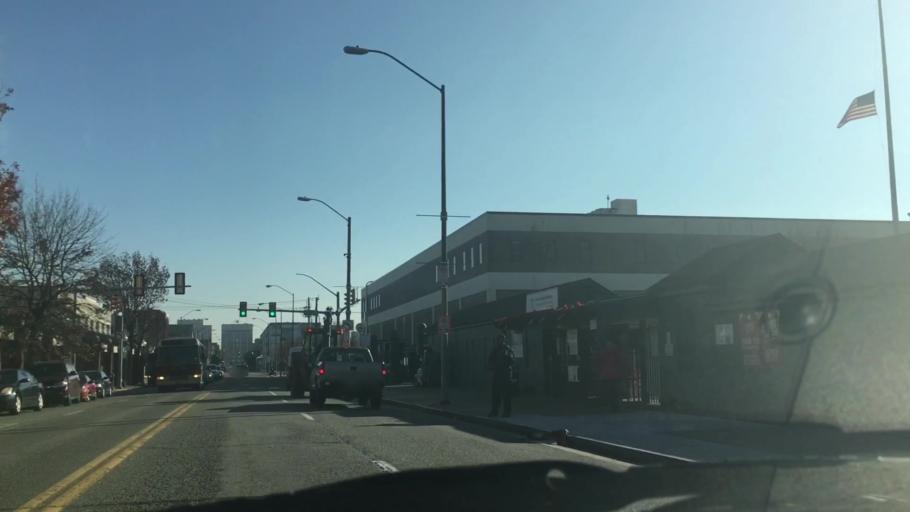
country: US
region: Virginia
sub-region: City of Newport News
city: Newport News
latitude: 36.9860
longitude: -76.4354
